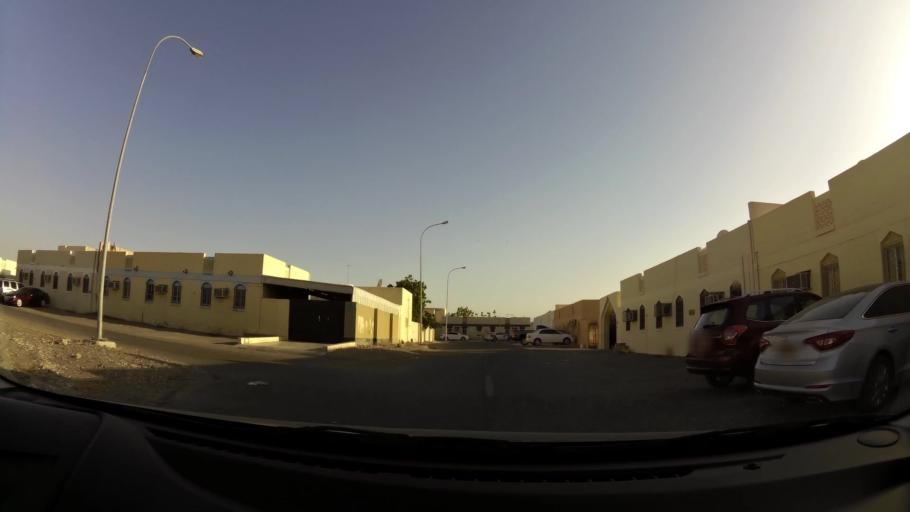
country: OM
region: Muhafazat Masqat
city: As Sib al Jadidah
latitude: 23.6265
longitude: 58.1914
